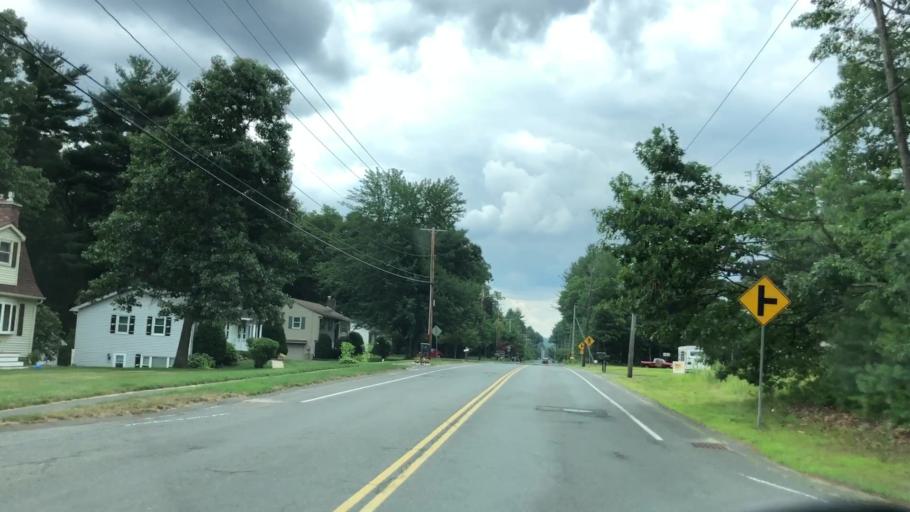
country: US
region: Massachusetts
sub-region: Hampshire County
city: Southampton
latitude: 42.2034
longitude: -72.6888
